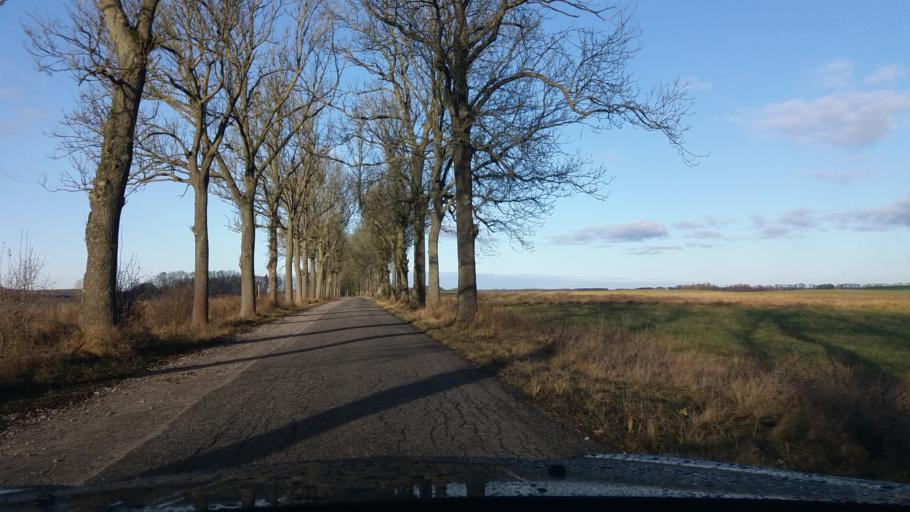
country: PL
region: West Pomeranian Voivodeship
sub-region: Powiat choszczenski
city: Drawno
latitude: 53.1865
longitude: 15.7962
